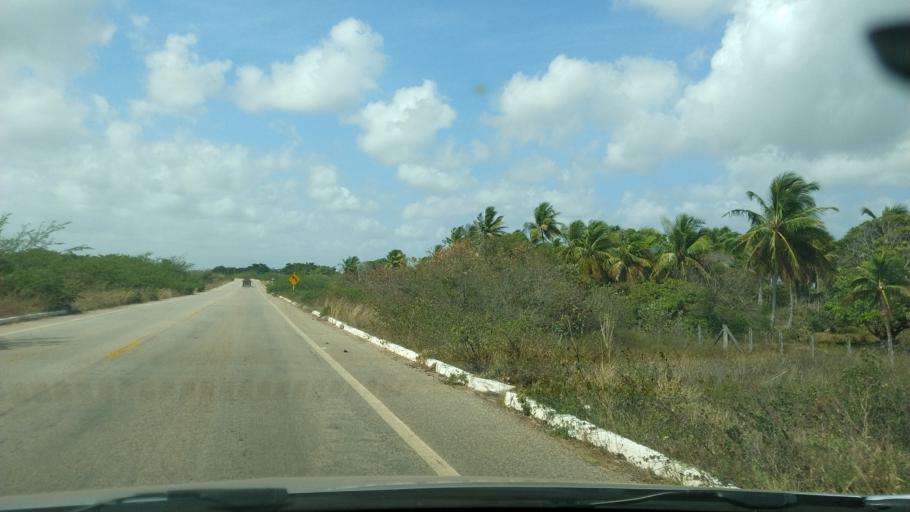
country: BR
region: Rio Grande do Norte
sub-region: Touros
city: Touros
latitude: -5.1788
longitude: -35.5102
